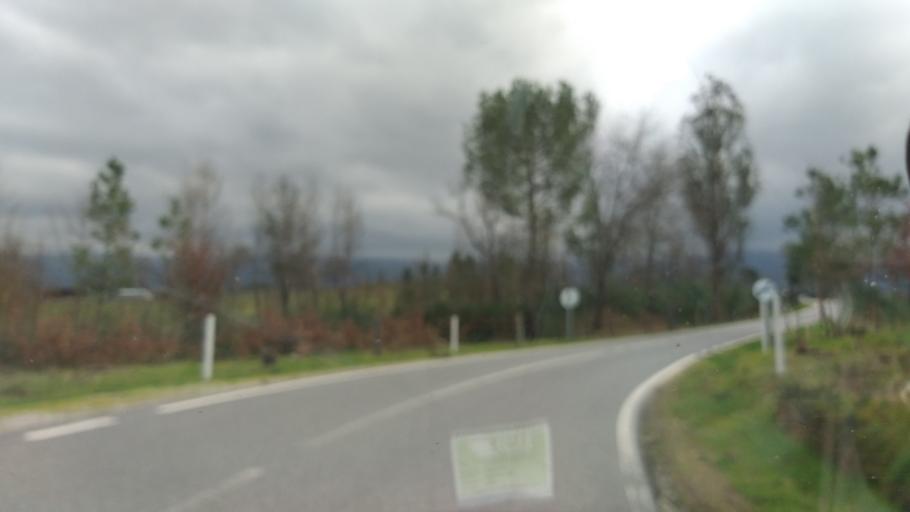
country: PT
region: Guarda
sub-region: Seia
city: Seia
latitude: 40.4845
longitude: -7.6541
